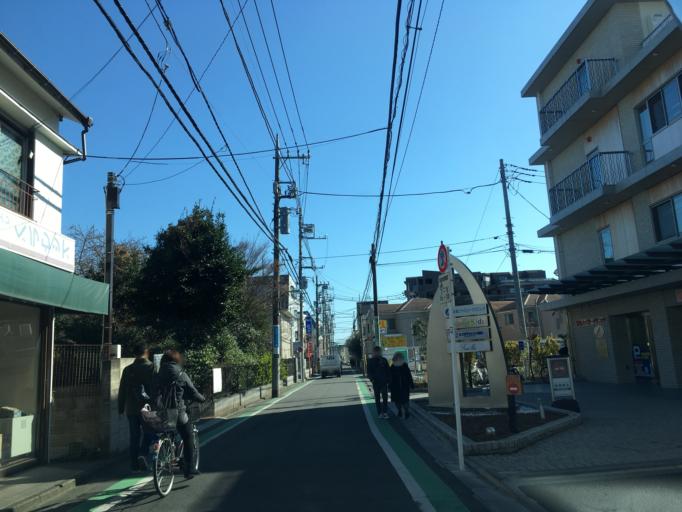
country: JP
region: Tokyo
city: Chofugaoka
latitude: 35.6538
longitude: 139.5682
